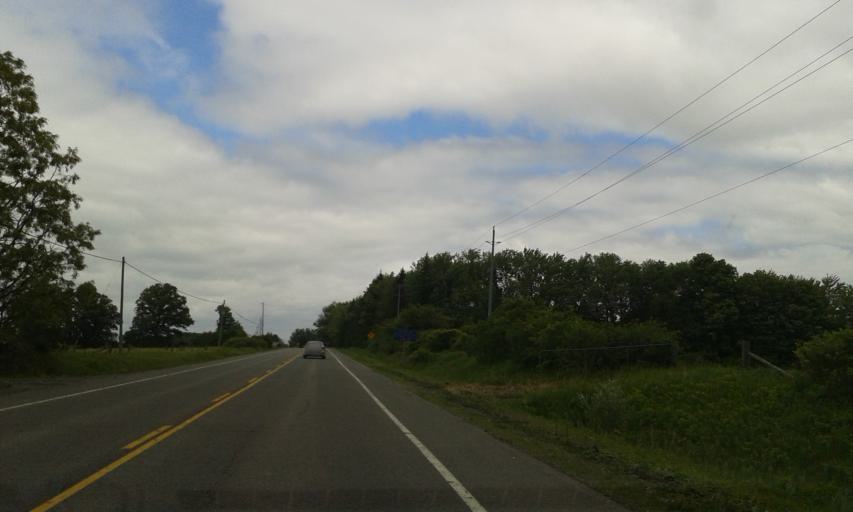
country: CA
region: Ontario
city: Picton
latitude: 44.0593
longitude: -77.0185
